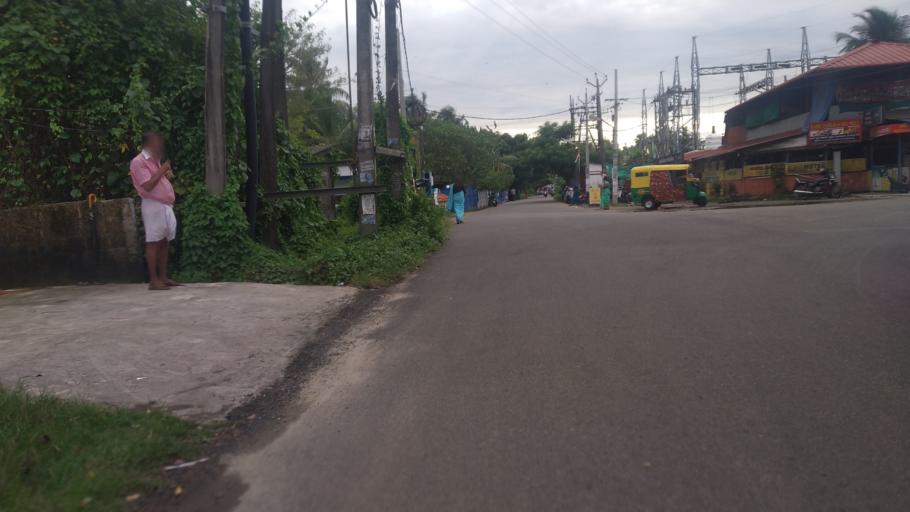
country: IN
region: Kerala
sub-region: Alappuzha
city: Arukutti
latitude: 9.8560
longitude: 76.2703
